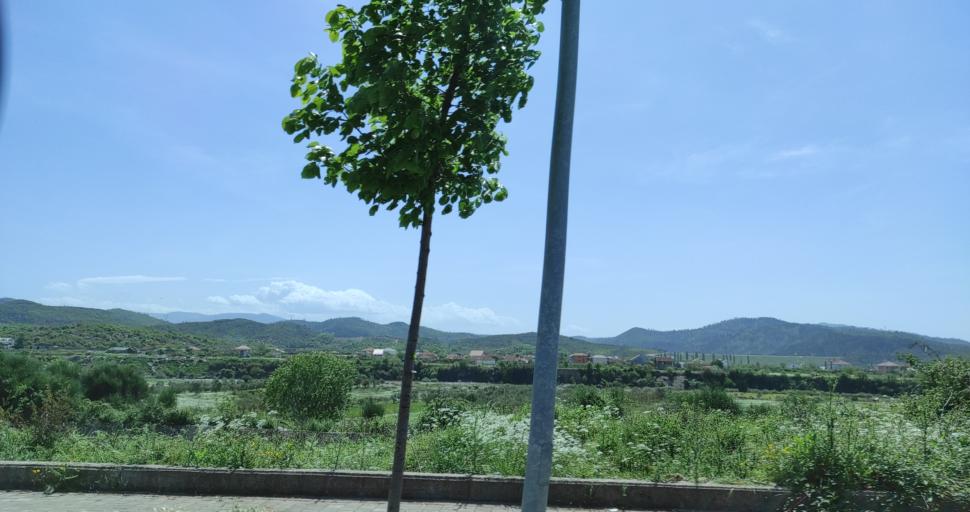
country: AL
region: Shkoder
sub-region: Rrethi i Shkodres
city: Guri i Zi
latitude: 42.1096
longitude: 19.5658
